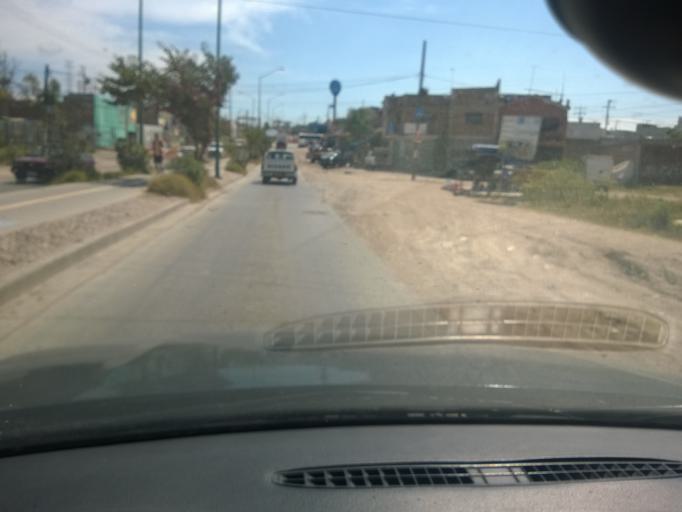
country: MX
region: Guanajuato
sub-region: Leon
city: Ejido la Joya
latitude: 21.1399
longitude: -101.7370
